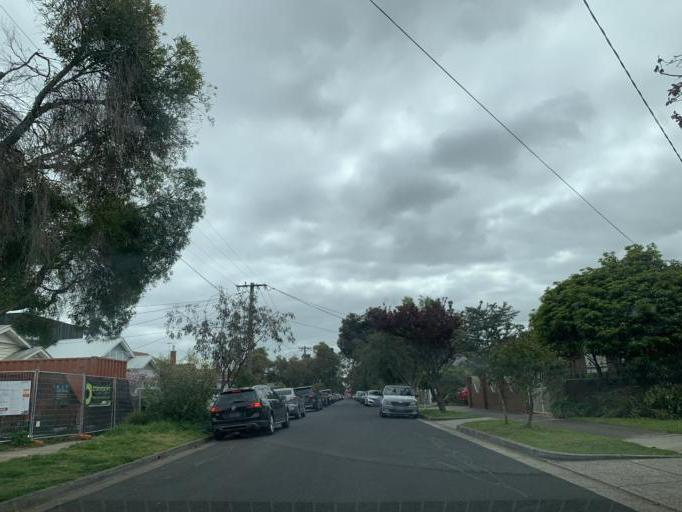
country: AU
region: Victoria
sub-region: Moreland
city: Pascoe Vale South
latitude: -37.7425
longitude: 144.9484
